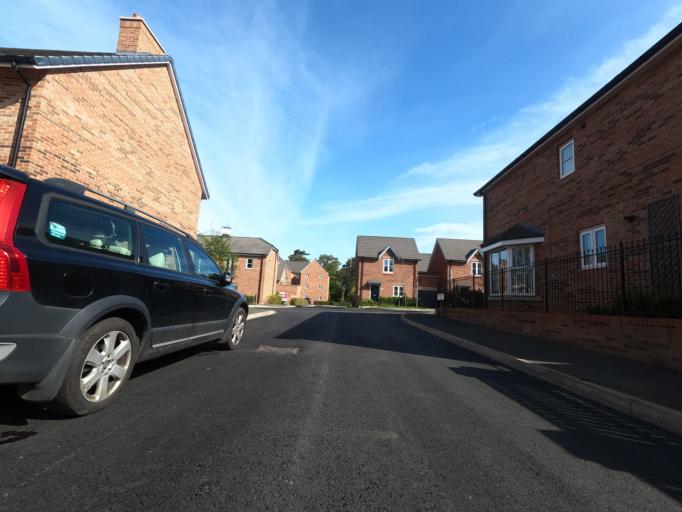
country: GB
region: England
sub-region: Northumberland
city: Morpeth
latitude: 55.1743
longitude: -1.6853
